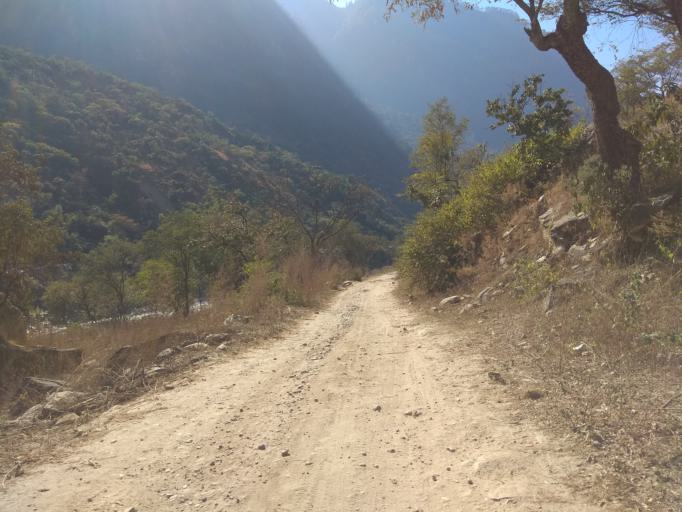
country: NP
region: Mid Western
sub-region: Bheri Zone
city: Dailekh
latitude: 29.2277
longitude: 81.6567
